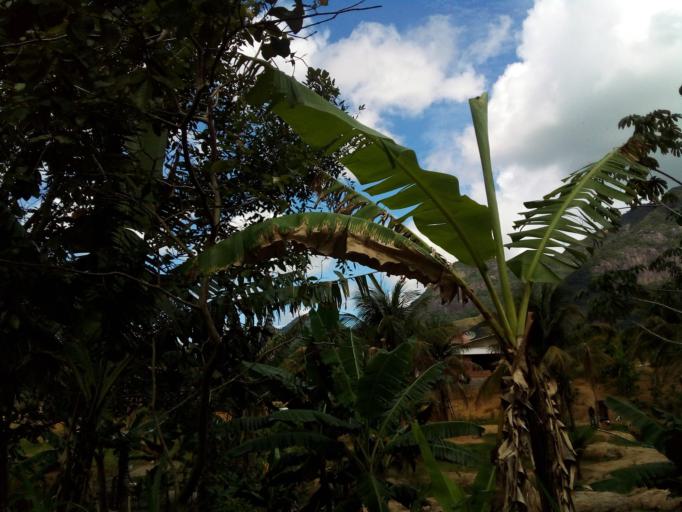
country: BR
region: Espirito Santo
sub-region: Ibiracu
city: Ibiracu
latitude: -19.8870
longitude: -40.3639
